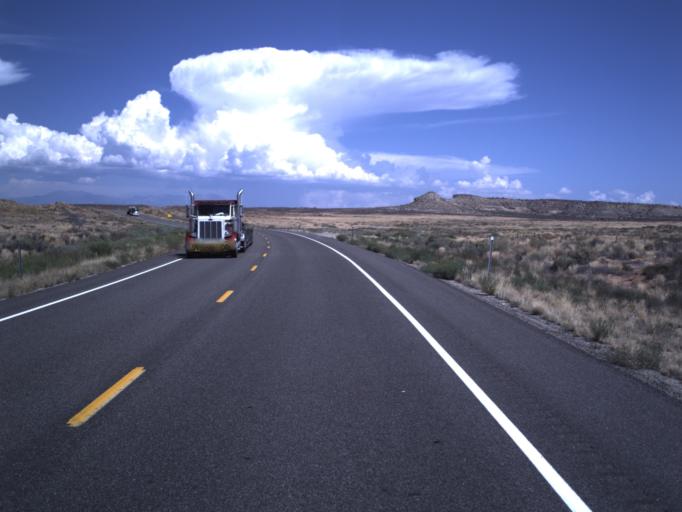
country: US
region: Utah
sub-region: San Juan County
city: Blanding
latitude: 37.3311
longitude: -109.5199
